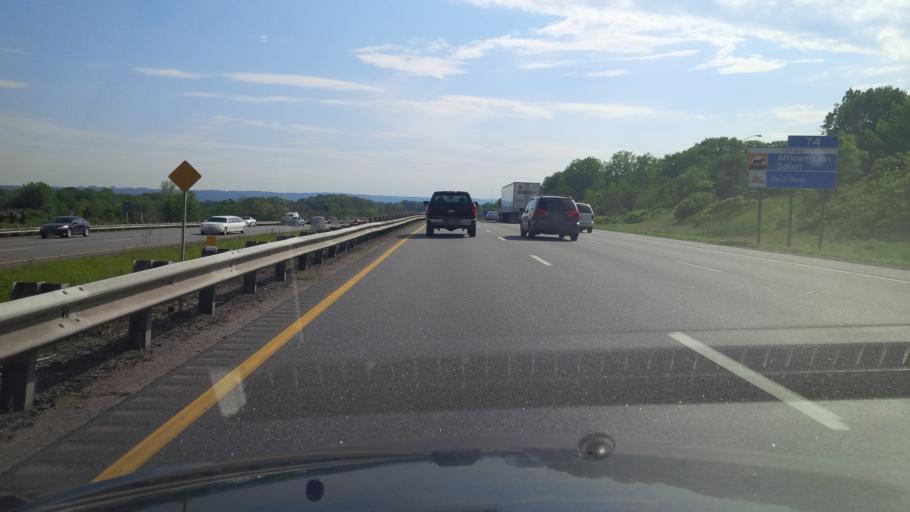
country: CA
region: Ontario
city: Hamilton
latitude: 43.3039
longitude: -79.8714
